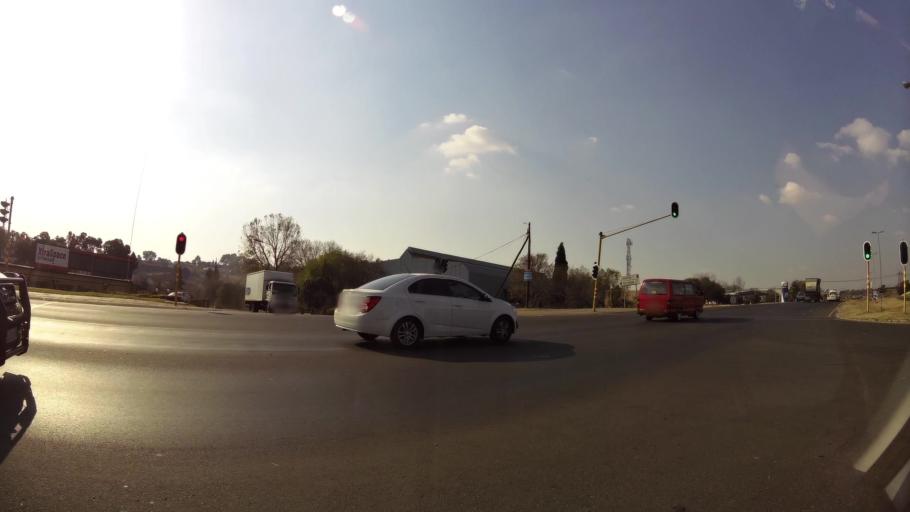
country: ZA
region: Gauteng
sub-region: City of Johannesburg Metropolitan Municipality
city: Modderfontein
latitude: -26.1050
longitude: 28.1714
